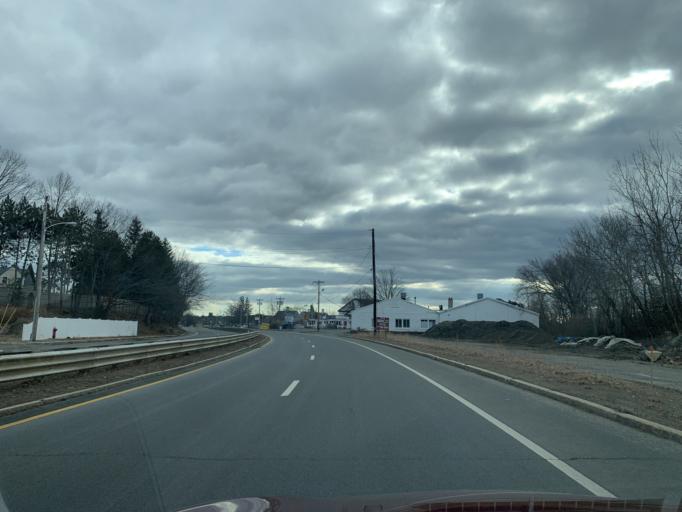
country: US
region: Massachusetts
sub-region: Essex County
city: Newburyport
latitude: 42.8024
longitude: -70.8790
